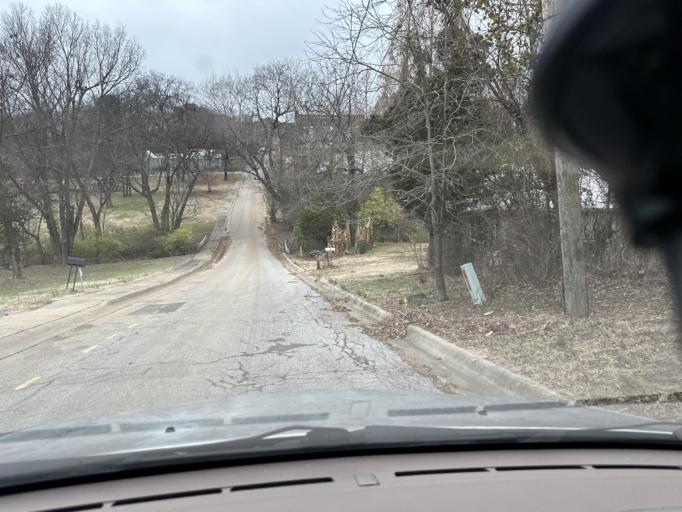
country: US
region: Arkansas
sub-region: Washington County
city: Fayetteville
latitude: 36.0620
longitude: -94.1549
